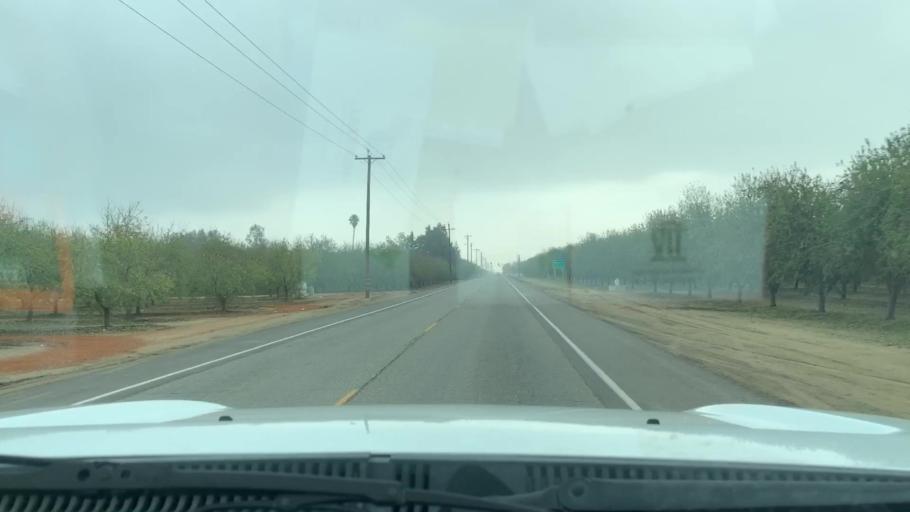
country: US
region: California
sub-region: Kern County
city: Wasco
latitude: 35.5580
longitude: -119.3373
